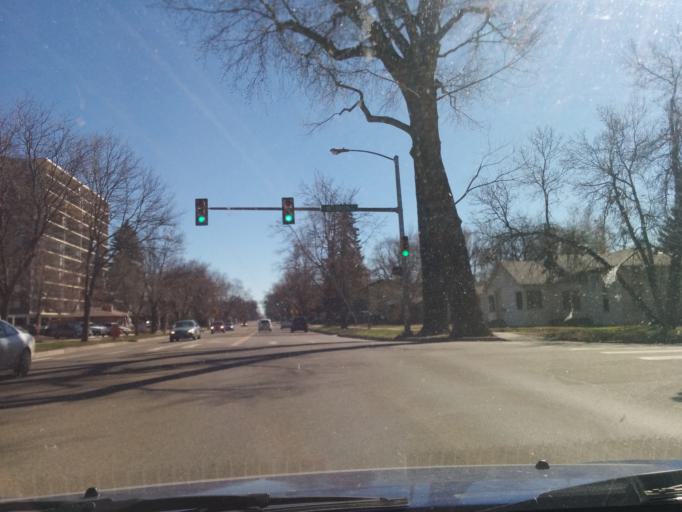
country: US
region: Colorado
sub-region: Larimer County
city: Fort Collins
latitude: 40.5814
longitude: -105.0827
